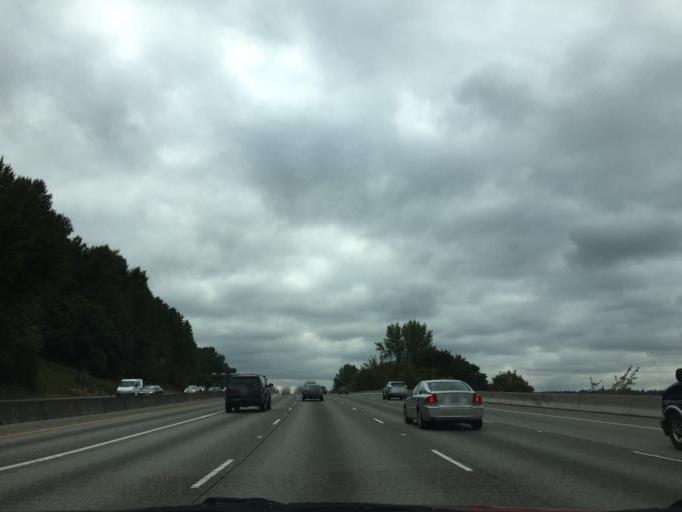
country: US
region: Washington
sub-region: King County
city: Riverton
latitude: 47.5219
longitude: -122.2913
